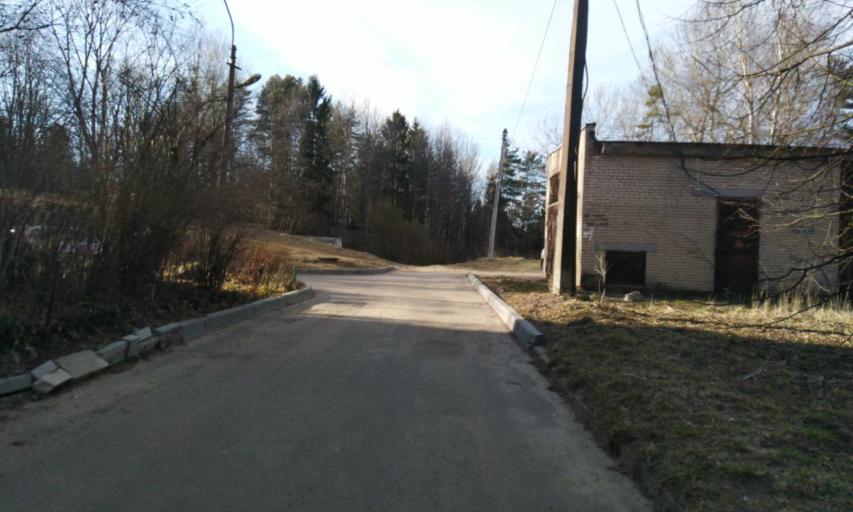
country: RU
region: Leningrad
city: Toksovo
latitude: 60.1247
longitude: 30.5014
